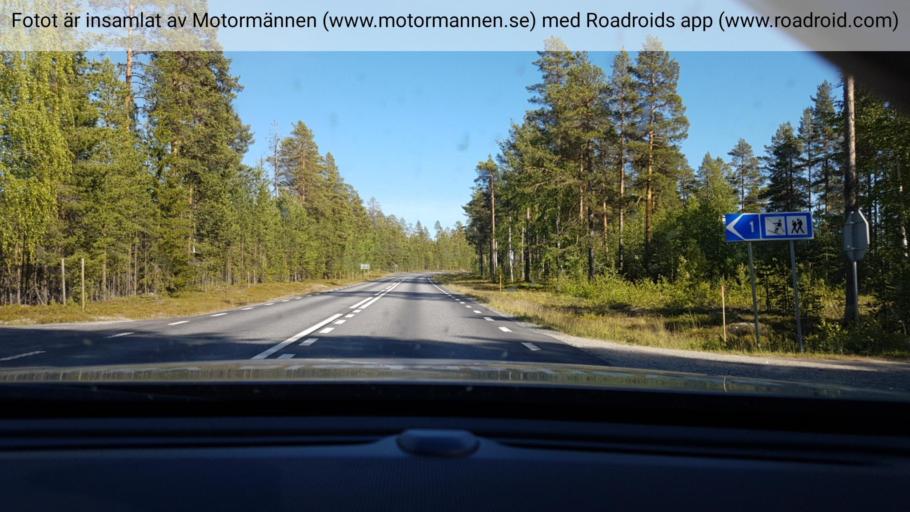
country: SE
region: Vaesterbotten
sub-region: Lycksele Kommun
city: Lycksele
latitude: 64.5217
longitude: 18.8243
